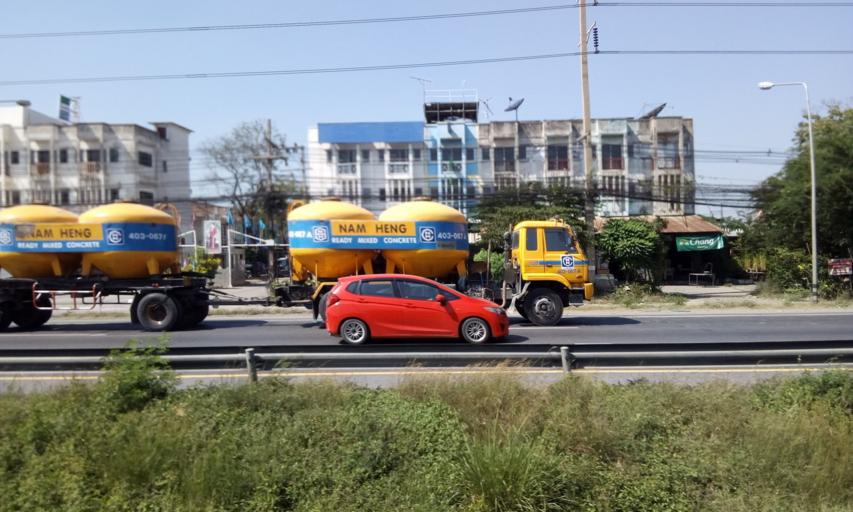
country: TH
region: Phra Nakhon Si Ayutthaya
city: Wang Noi
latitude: 14.2125
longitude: 100.6804
